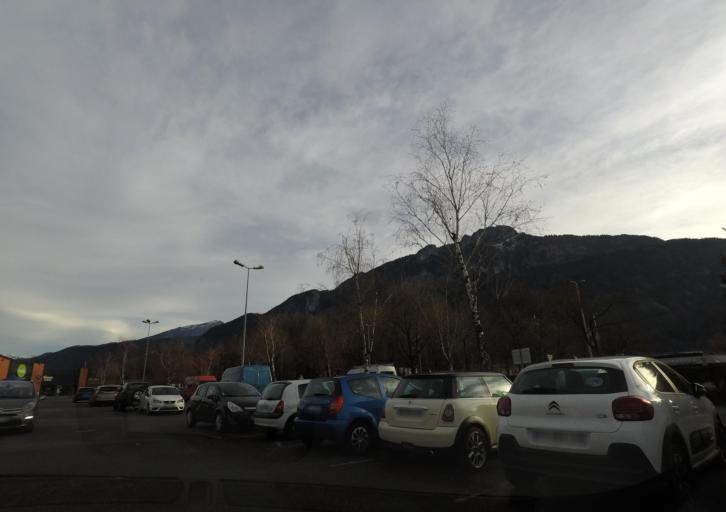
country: FR
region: Rhone-Alpes
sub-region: Departement de la Haute-Savoie
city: Bonneville
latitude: 46.0738
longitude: 6.4093
